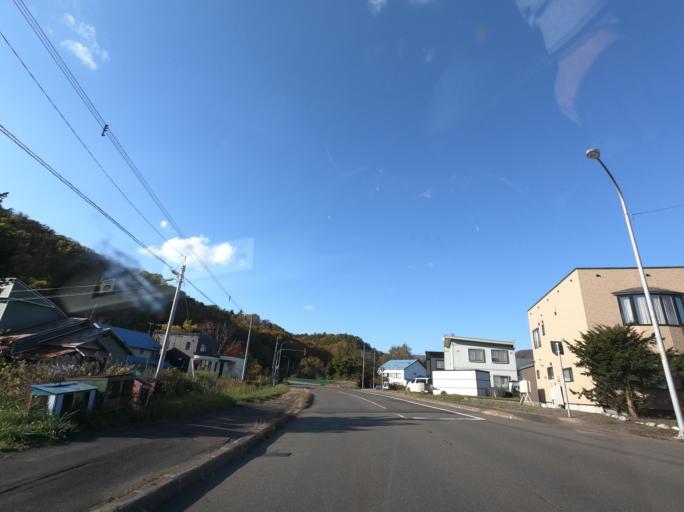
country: JP
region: Hokkaido
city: Iwamizawa
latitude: 42.9984
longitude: 142.0061
